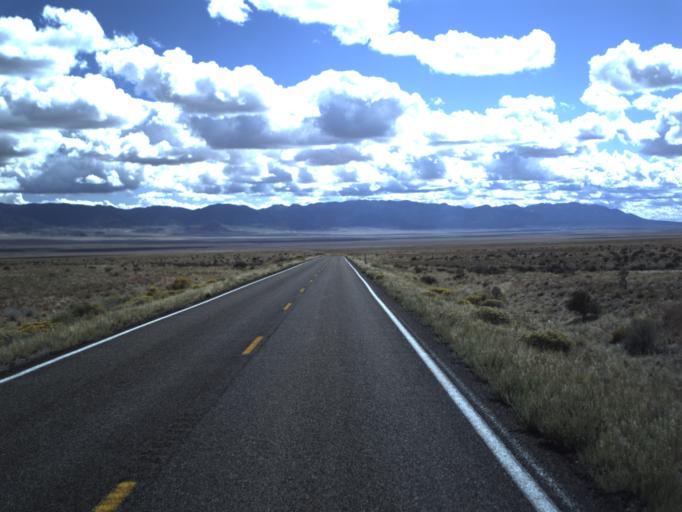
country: US
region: Utah
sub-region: Beaver County
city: Milford
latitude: 38.5872
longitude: -113.8157
